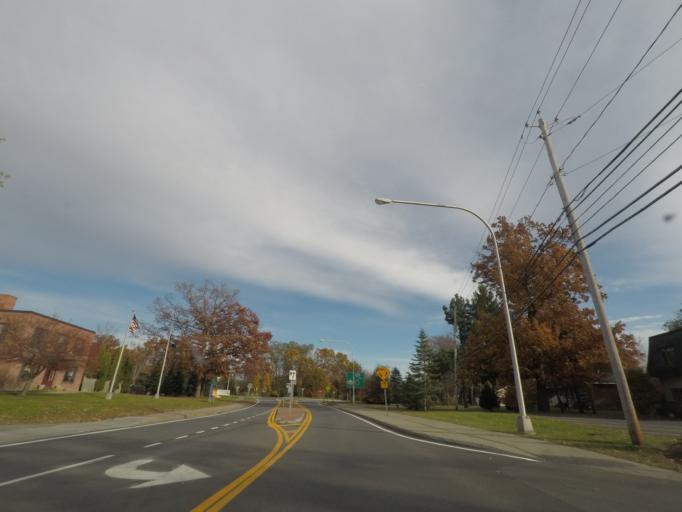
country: US
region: New York
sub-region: Albany County
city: Voorheesville
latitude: 42.6493
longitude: -73.9225
